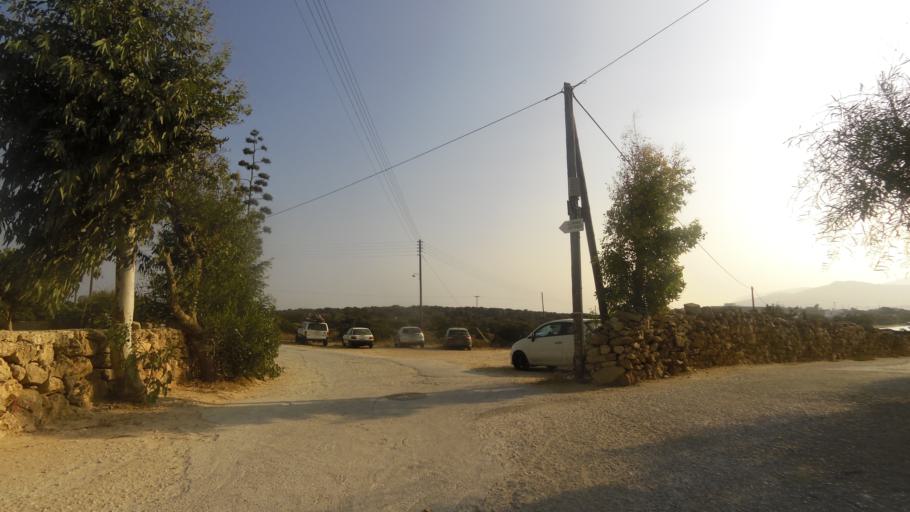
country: GR
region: South Aegean
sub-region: Nomos Kykladon
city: Antiparos
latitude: 37.0437
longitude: 25.0837
